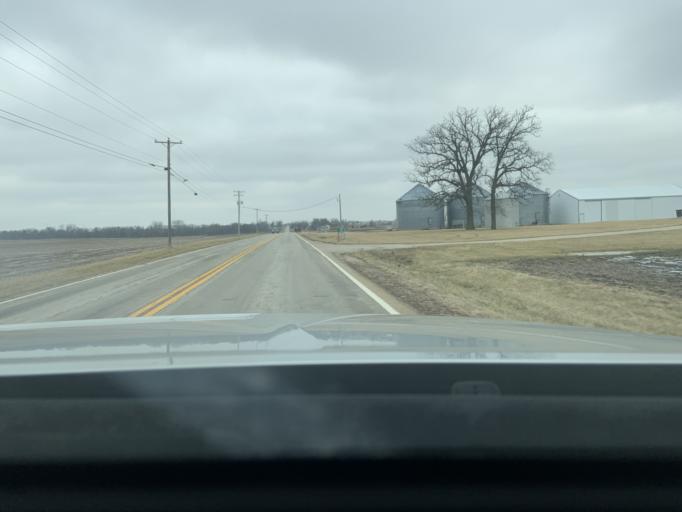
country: US
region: Illinois
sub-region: LaSalle County
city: Seneca
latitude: 41.3483
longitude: -88.6118
